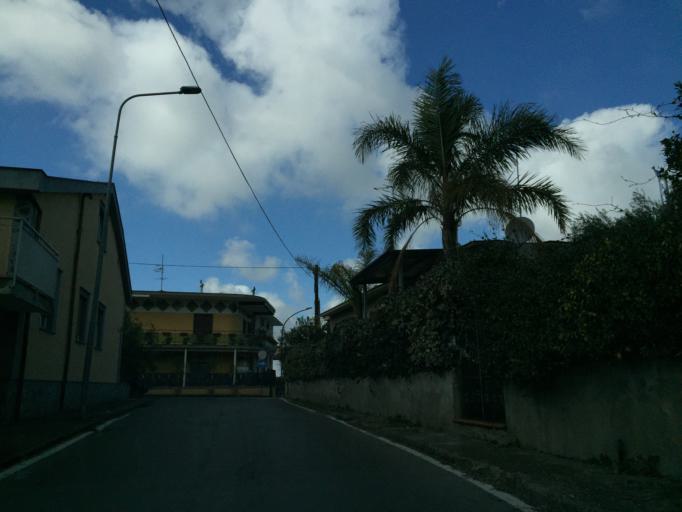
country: IT
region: Campania
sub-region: Provincia di Napoli
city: Massa di Somma
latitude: 40.8438
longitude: 14.3737
